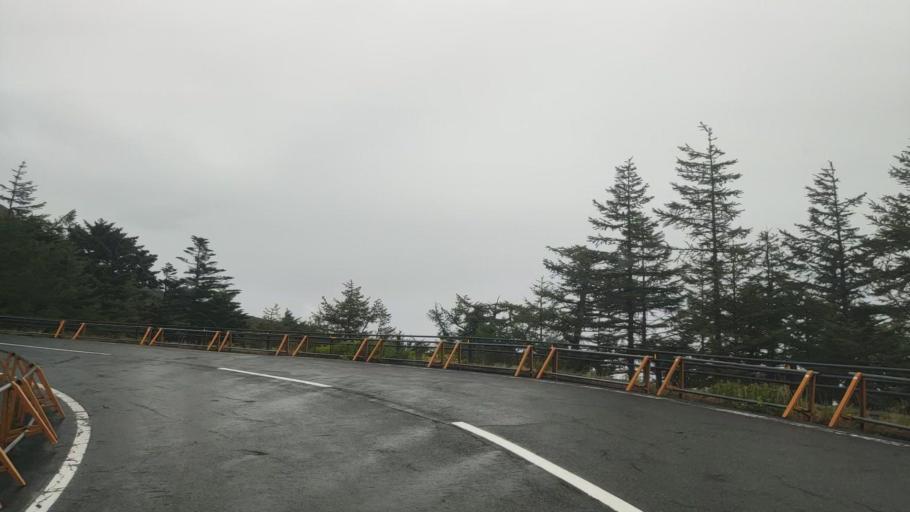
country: JP
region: Yamanashi
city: Fujikawaguchiko
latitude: 35.3339
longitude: 138.7357
